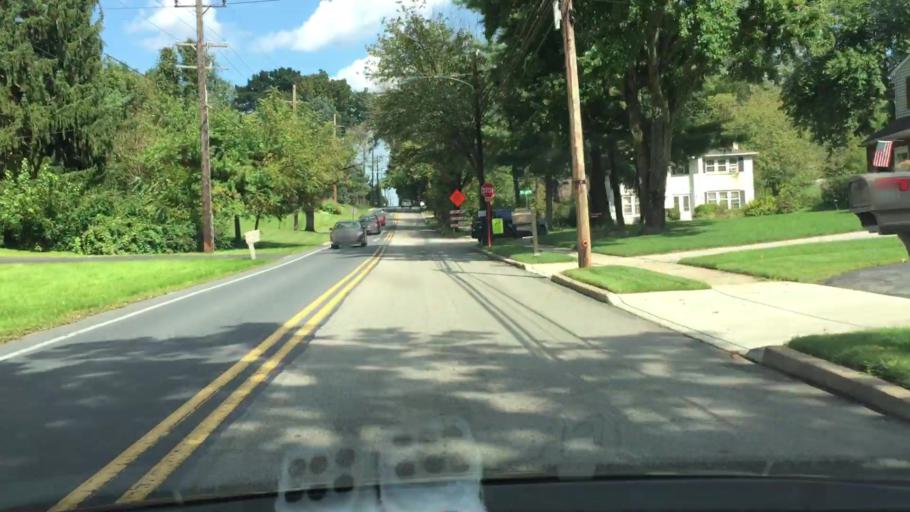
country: US
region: Pennsylvania
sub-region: Montgomery County
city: Blue Bell
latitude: 40.1389
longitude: -75.3025
